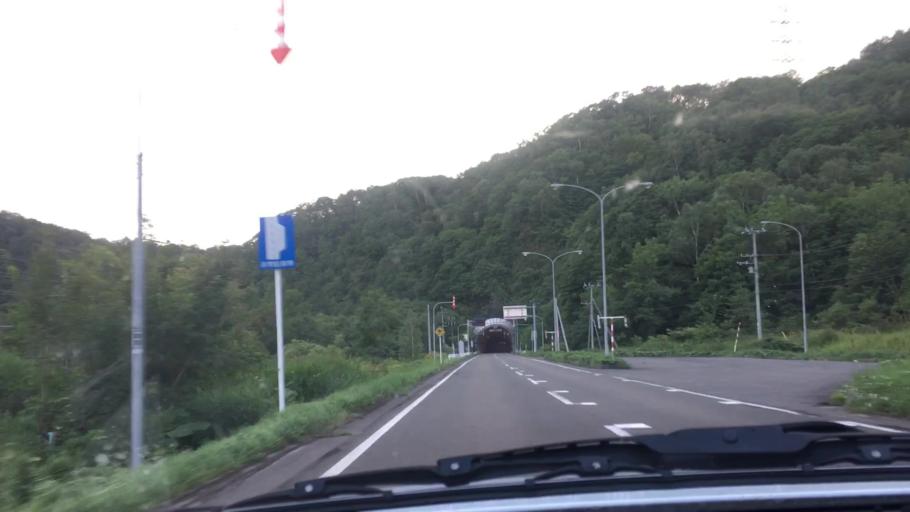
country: JP
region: Hokkaido
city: Shimo-furano
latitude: 43.0449
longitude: 142.4704
